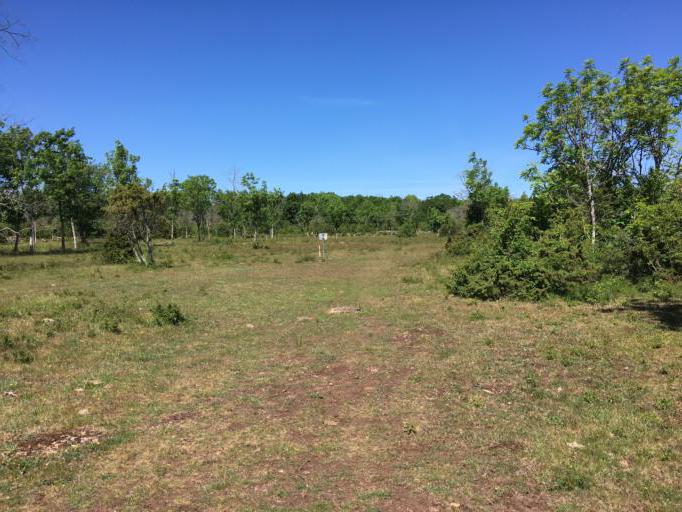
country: SE
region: Kalmar
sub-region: Borgholms Kommun
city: Borgholm
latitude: 56.7478
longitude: 16.6054
